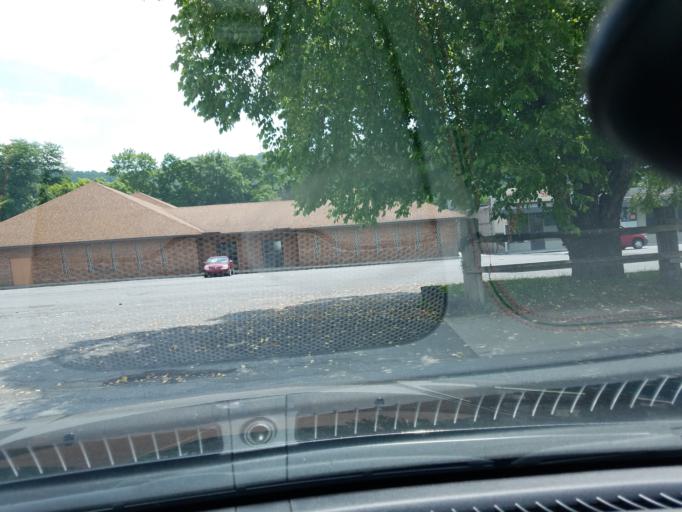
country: US
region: Pennsylvania
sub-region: Cambria County
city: Johnstown
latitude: 40.3508
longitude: -78.9440
